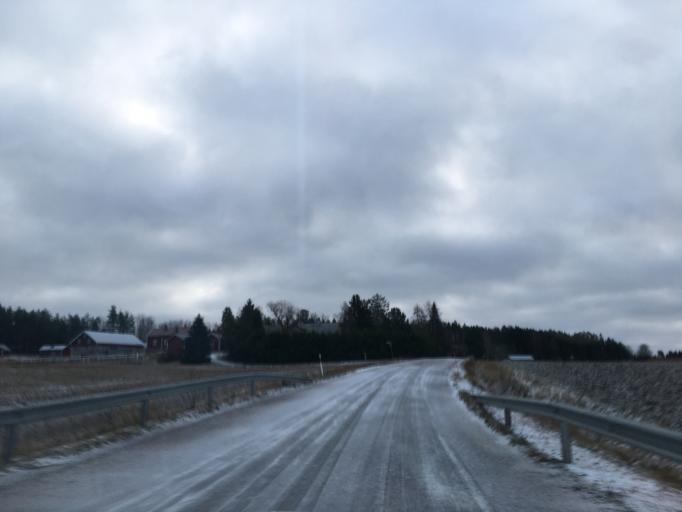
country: FI
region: Varsinais-Suomi
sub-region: Loimaa
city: Aura
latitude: 60.5875
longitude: 22.5332
